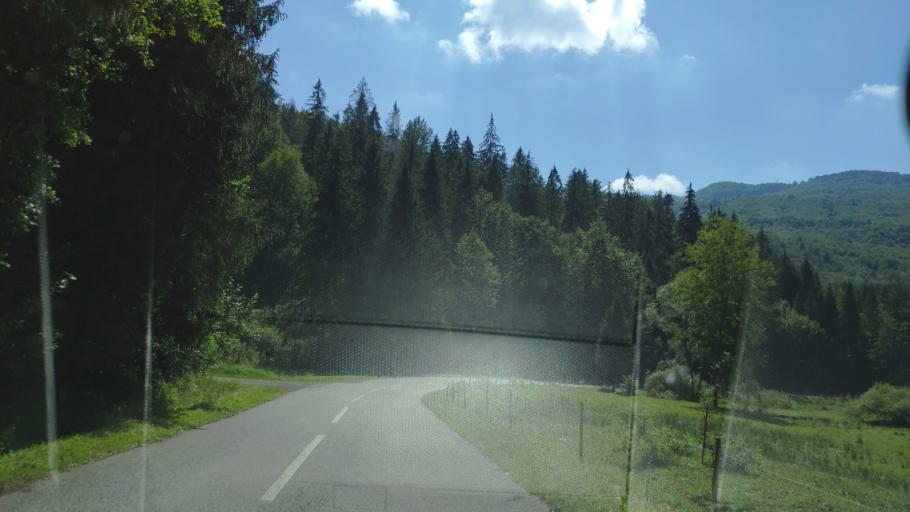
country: PL
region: Subcarpathian Voivodeship
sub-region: Powiat leski
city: Cisna
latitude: 49.0678
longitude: 22.3978
